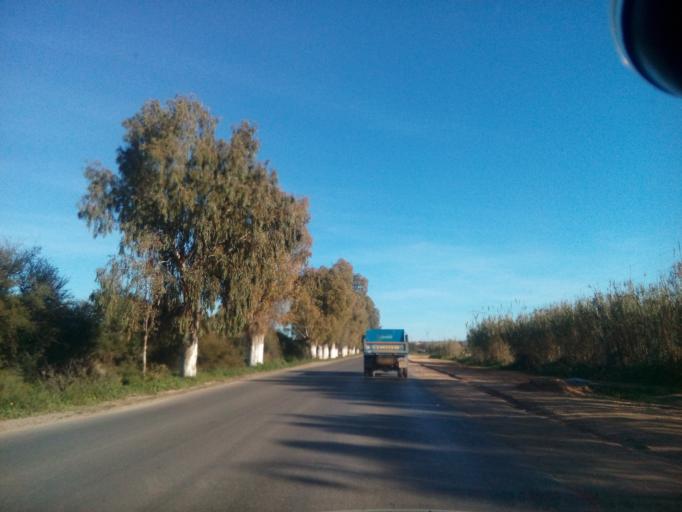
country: DZ
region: Mostaganem
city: Mostaganem
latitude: 35.9009
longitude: 0.2188
